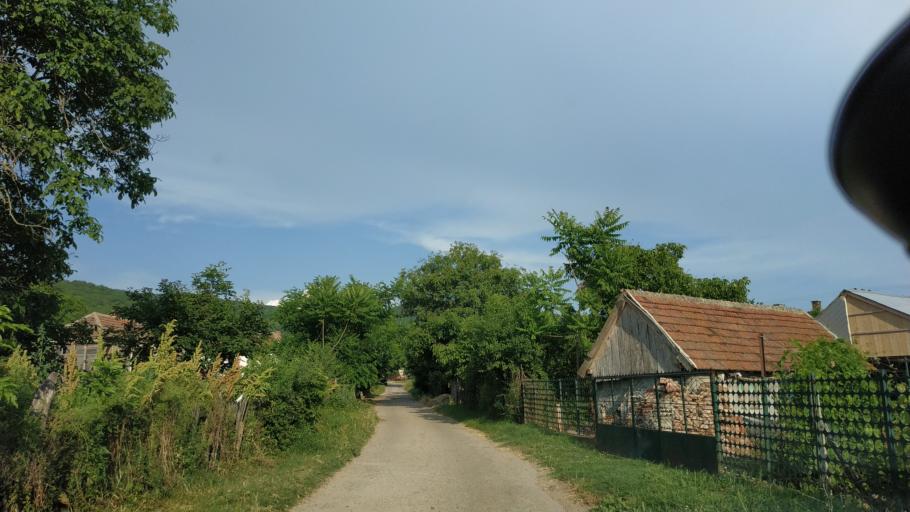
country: RS
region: Central Serbia
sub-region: Nisavski Okrug
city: Aleksinac
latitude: 43.6071
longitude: 21.6894
